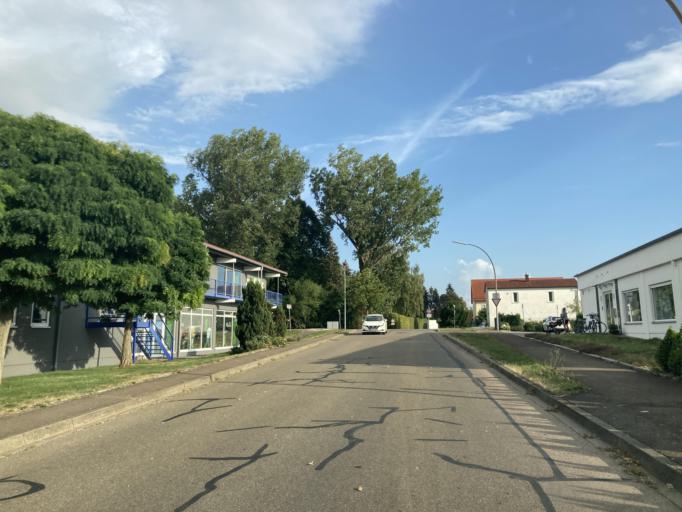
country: DE
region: Bavaria
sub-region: Swabia
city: Noerdlingen
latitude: 48.8585
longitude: 10.5120
